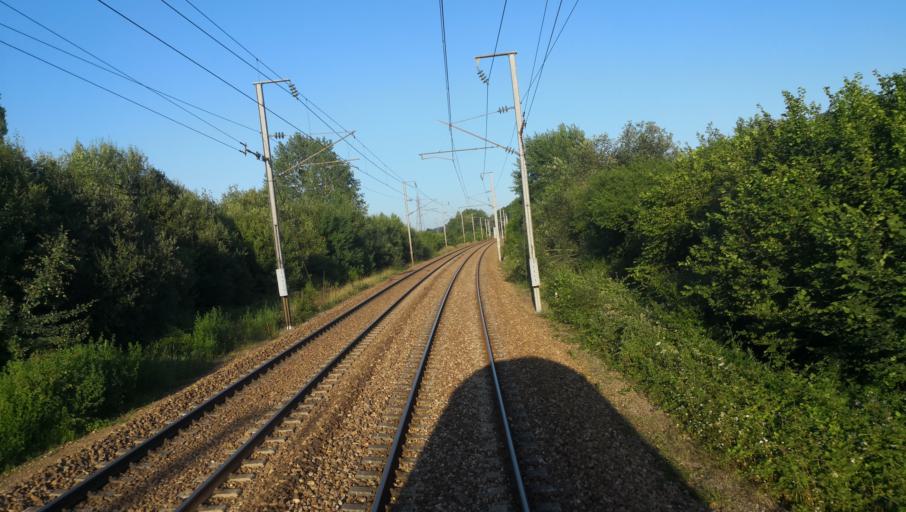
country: FR
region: Lower Normandy
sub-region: Departement du Calvados
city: Beuvillers
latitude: 49.1260
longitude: 0.2899
